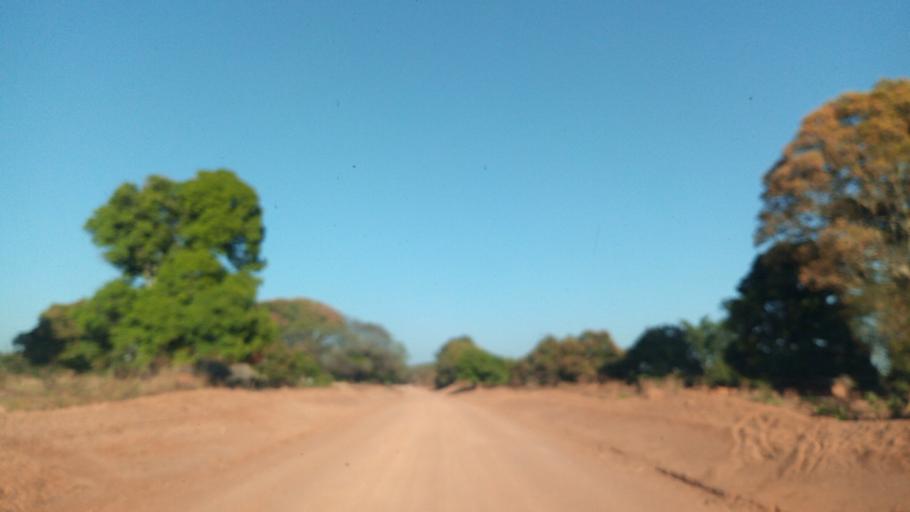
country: ZM
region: Luapula
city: Mwense
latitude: -10.4405
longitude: 28.5855
